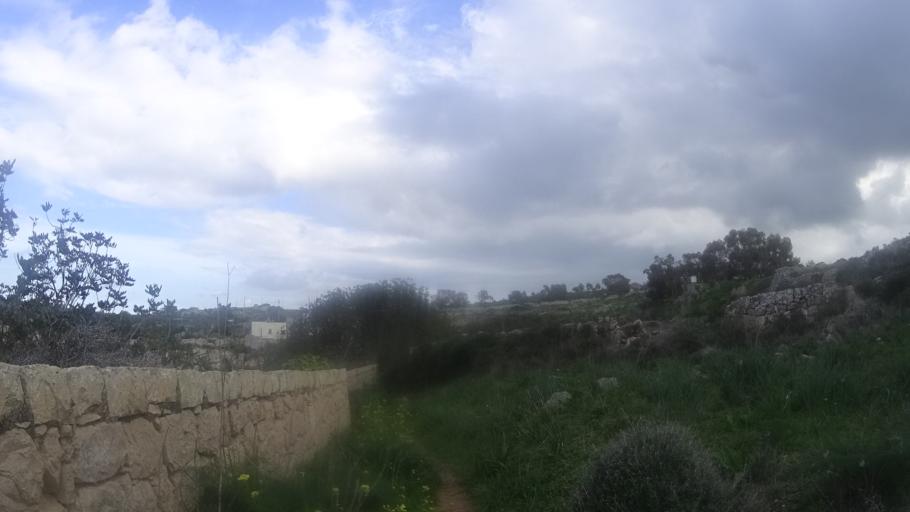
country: MT
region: L-Imgarr
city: Imgarr
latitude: 35.9020
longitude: 14.3669
